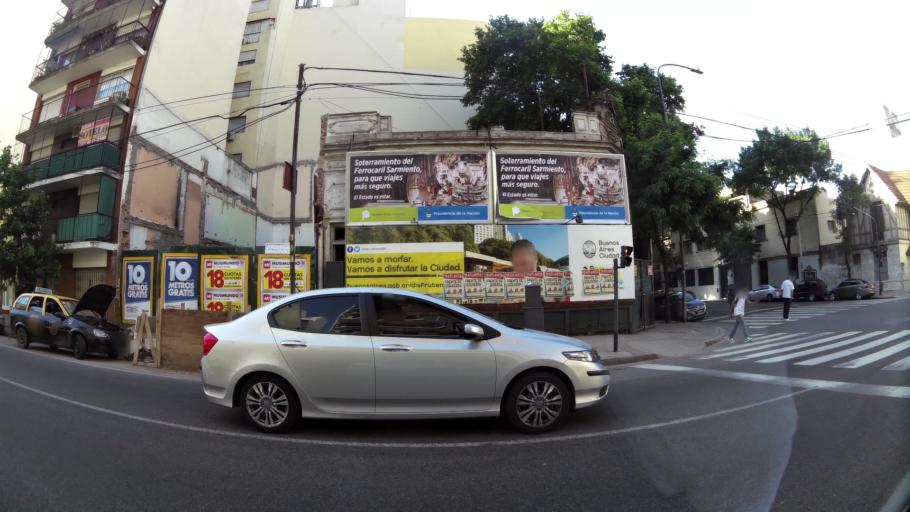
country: AR
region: Buenos Aires F.D.
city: Villa Santa Rita
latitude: -34.6225
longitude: -58.4598
